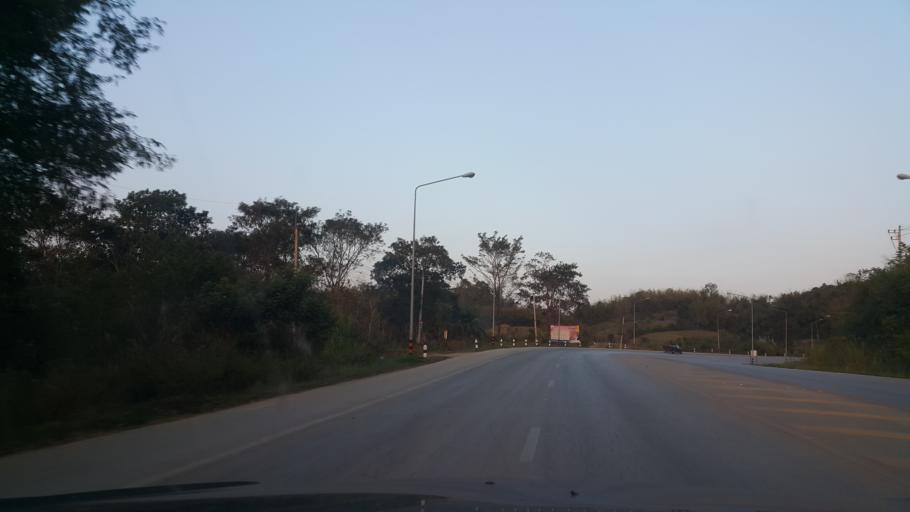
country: TH
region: Loei
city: Loei
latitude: 17.4930
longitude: 101.6896
